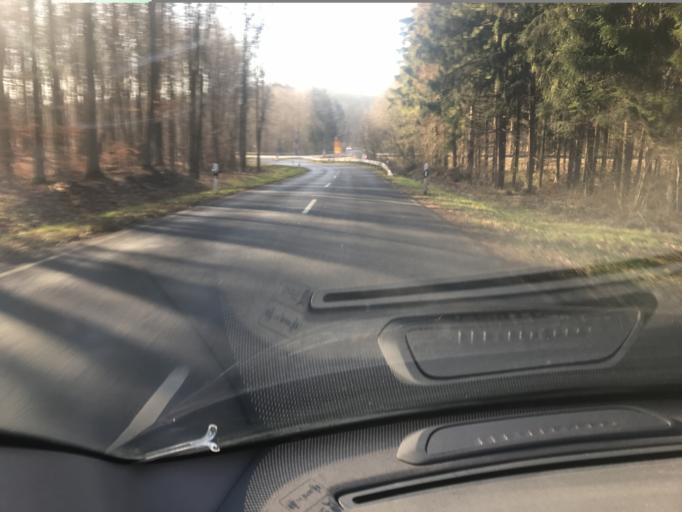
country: DE
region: Rheinland-Pfalz
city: Dreikirchen
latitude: 50.4399
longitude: 7.9381
